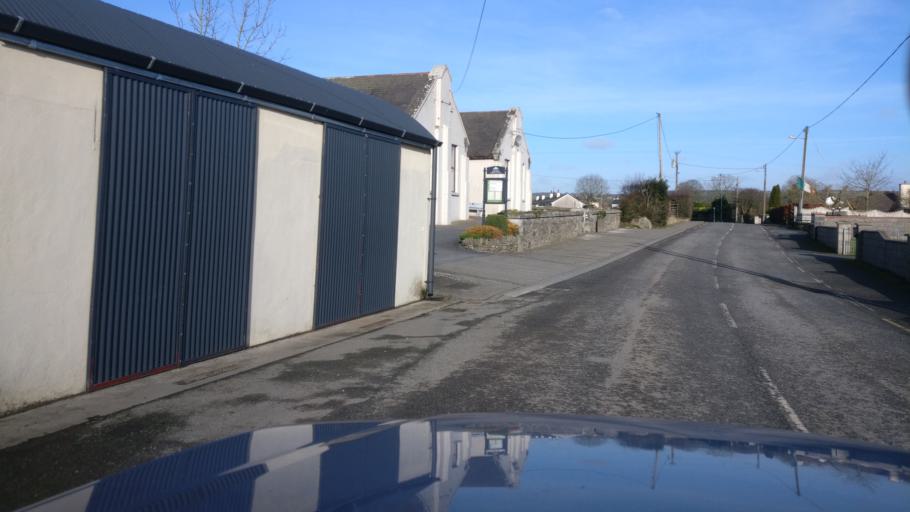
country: IE
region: Leinster
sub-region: Kilkenny
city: Castlecomer
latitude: 52.8580
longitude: -7.1652
